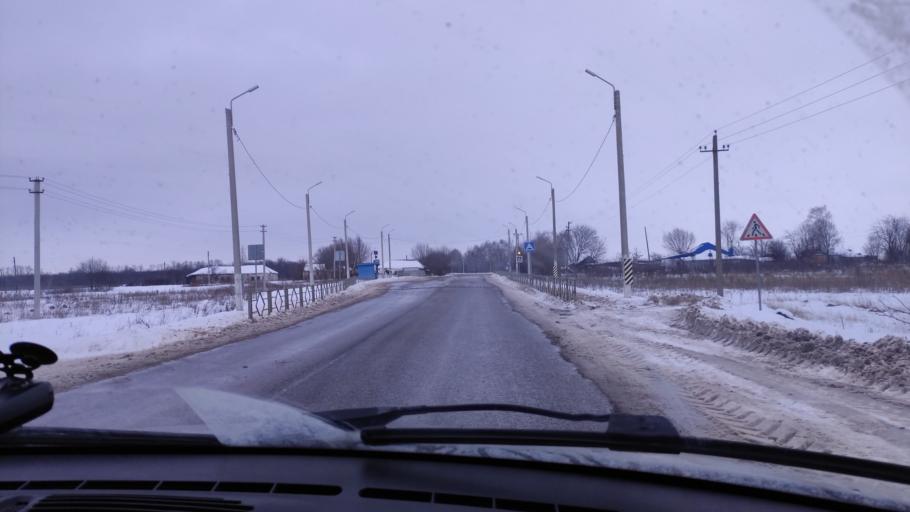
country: RU
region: Tambov
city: Pervomayskiy
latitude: 53.3033
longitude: 40.3796
